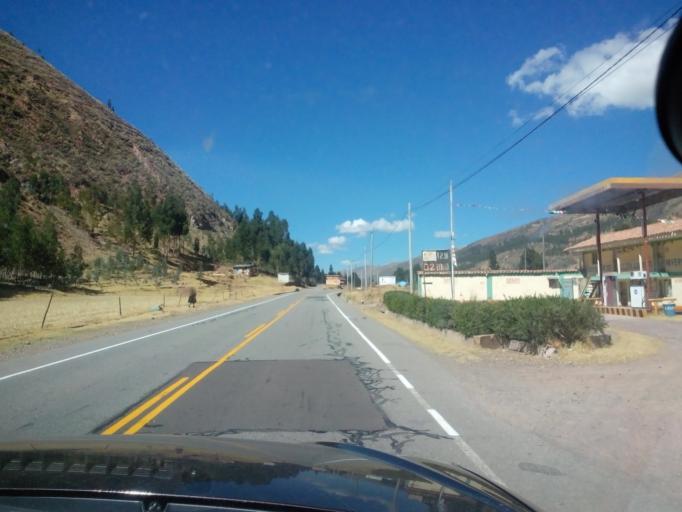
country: PE
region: Cusco
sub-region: Provincia de Canchis
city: Checacupe
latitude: -14.0167
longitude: -71.4571
